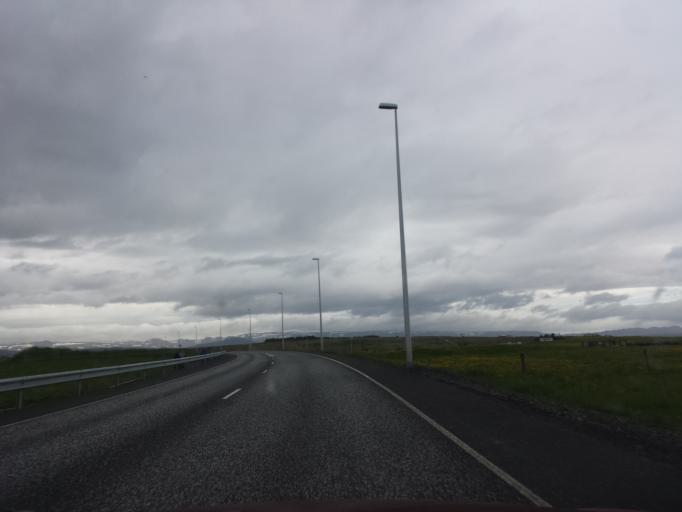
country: IS
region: Capital Region
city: Alftanes
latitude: 64.0983
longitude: -22.0058
